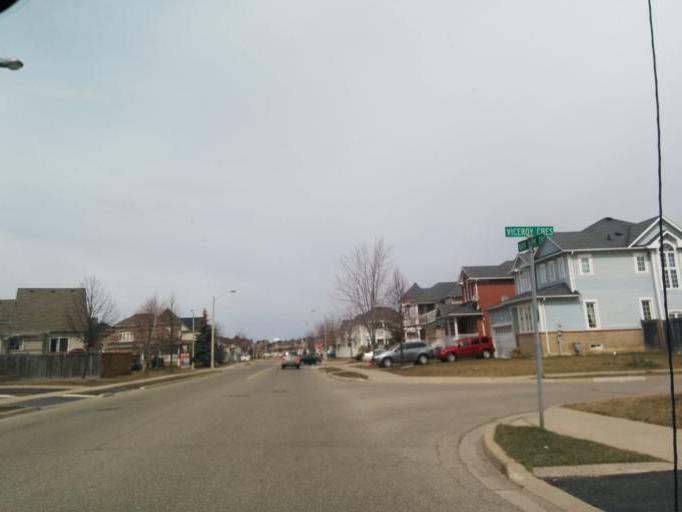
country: CA
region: Ontario
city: Brampton
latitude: 43.7147
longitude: -79.8187
